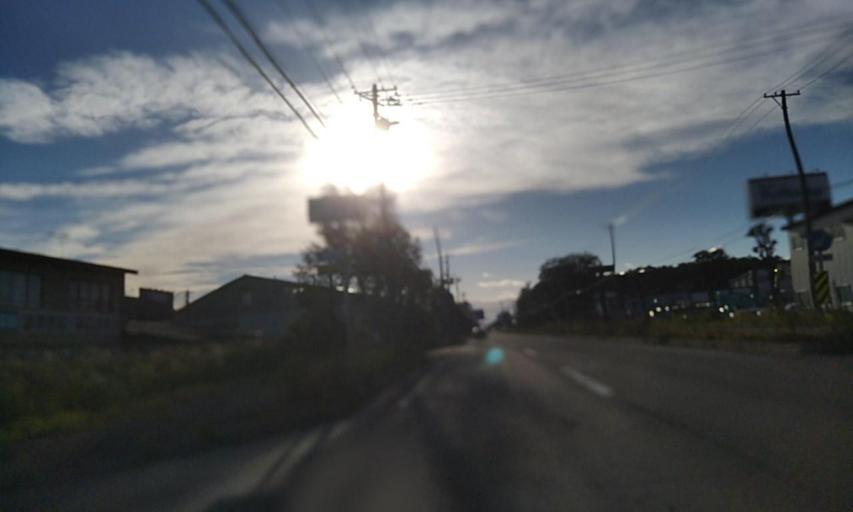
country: JP
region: Hokkaido
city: Obihiro
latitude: 42.9276
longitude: 143.1467
